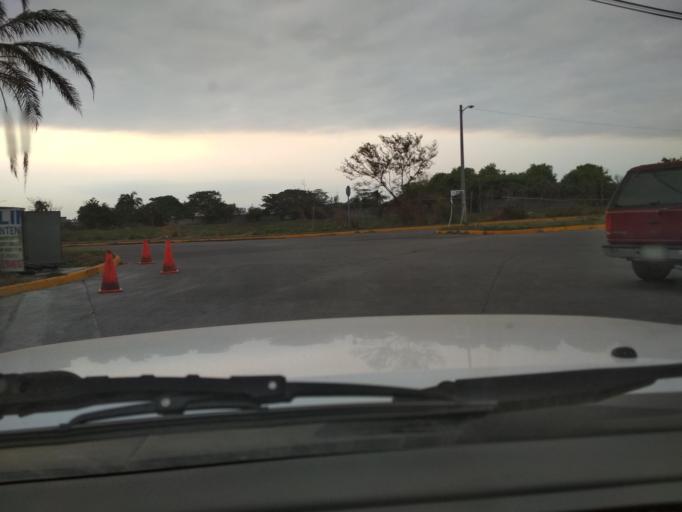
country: MX
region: Veracruz
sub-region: Medellin
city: Fraccionamiento Arboledas San Ramon
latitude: 19.0935
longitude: -96.1548
